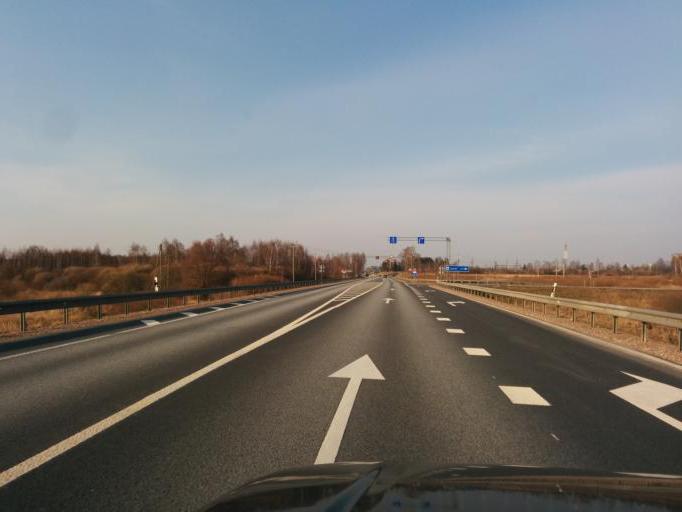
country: LV
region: Lecava
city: Iecava
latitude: 56.6226
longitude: 24.2194
